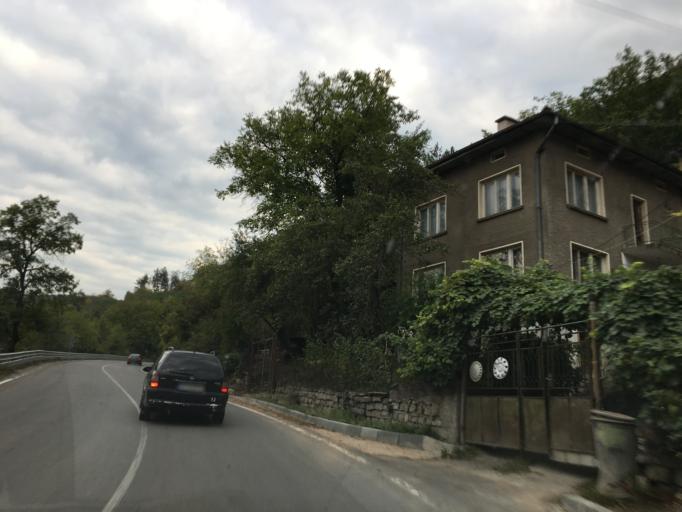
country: BG
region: Sofiya
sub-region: Obshtina Svoge
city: Svoge
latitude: 43.0017
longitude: 23.3457
